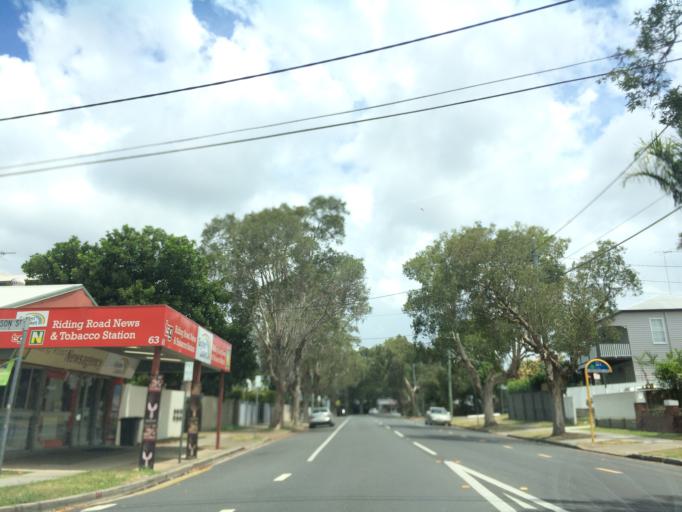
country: AU
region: Queensland
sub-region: Brisbane
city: Balmoral
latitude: -27.4663
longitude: 153.0645
